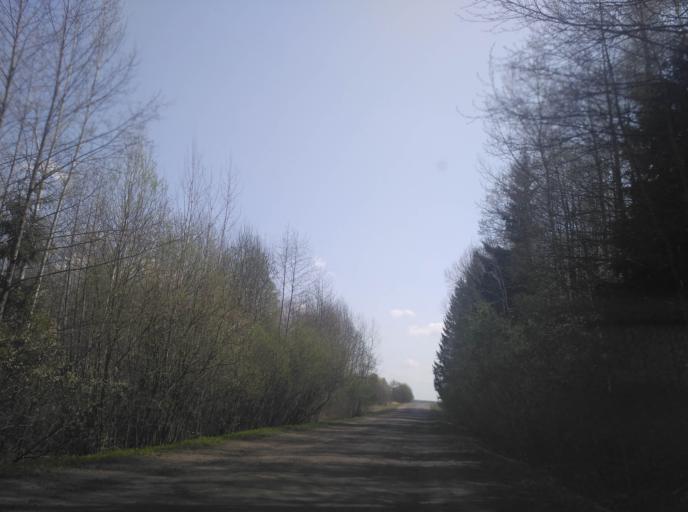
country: BY
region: Minsk
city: Loshnitsa
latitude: 54.4923
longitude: 28.7208
